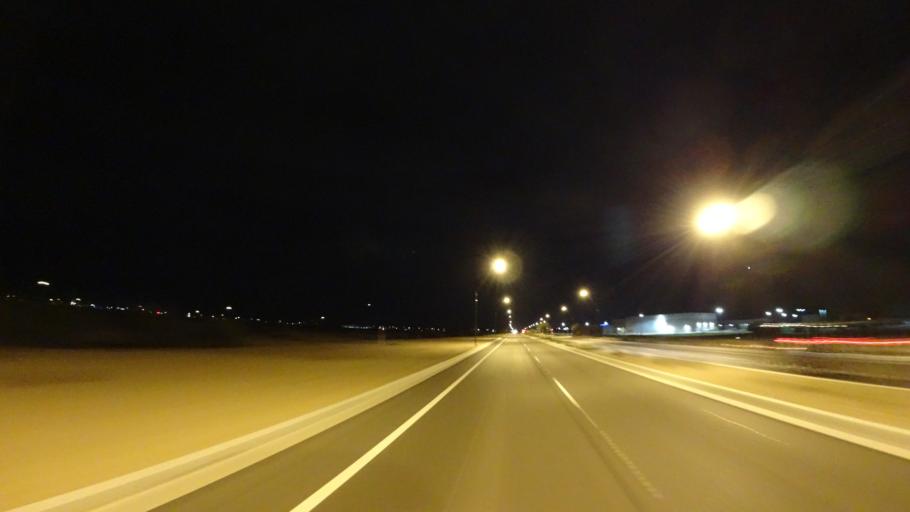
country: US
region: Arizona
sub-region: Maricopa County
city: Queen Creek
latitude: 33.2643
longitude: -111.6478
